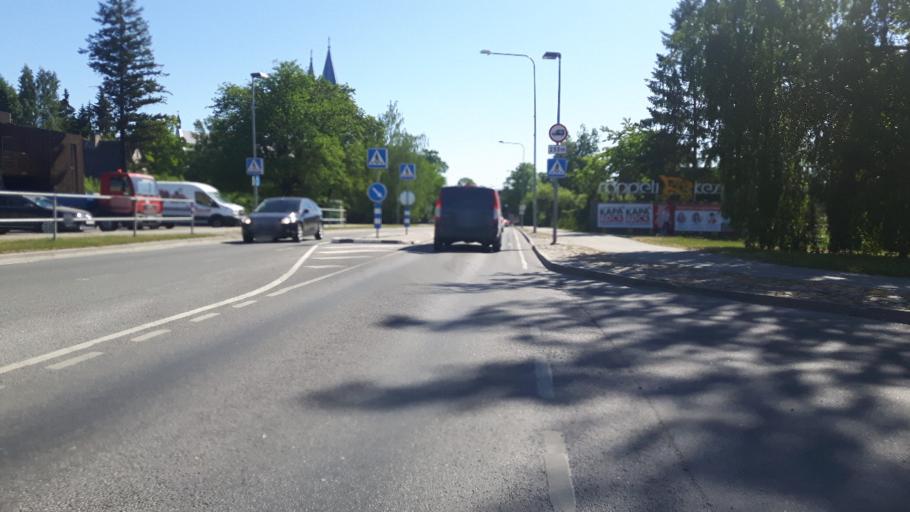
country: EE
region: Raplamaa
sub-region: Rapla vald
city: Rapla
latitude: 59.0094
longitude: 24.7956
